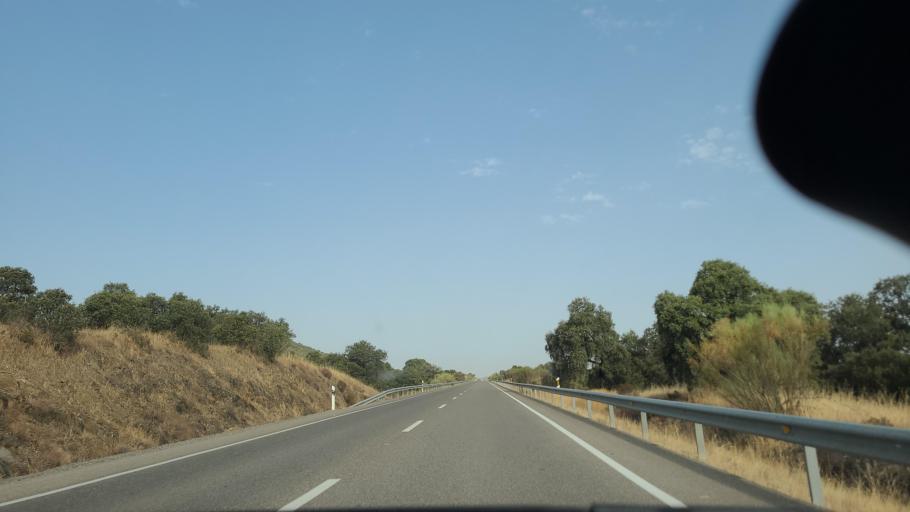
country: ES
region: Andalusia
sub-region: Province of Cordoba
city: Belmez
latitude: 38.2197
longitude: -5.1505
